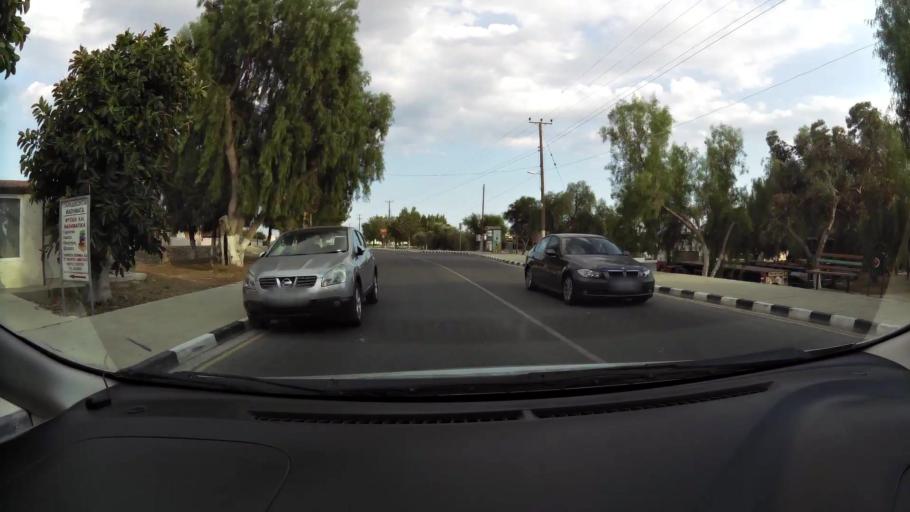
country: CY
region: Larnaka
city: Dhromolaxia
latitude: 34.8710
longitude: 33.5897
